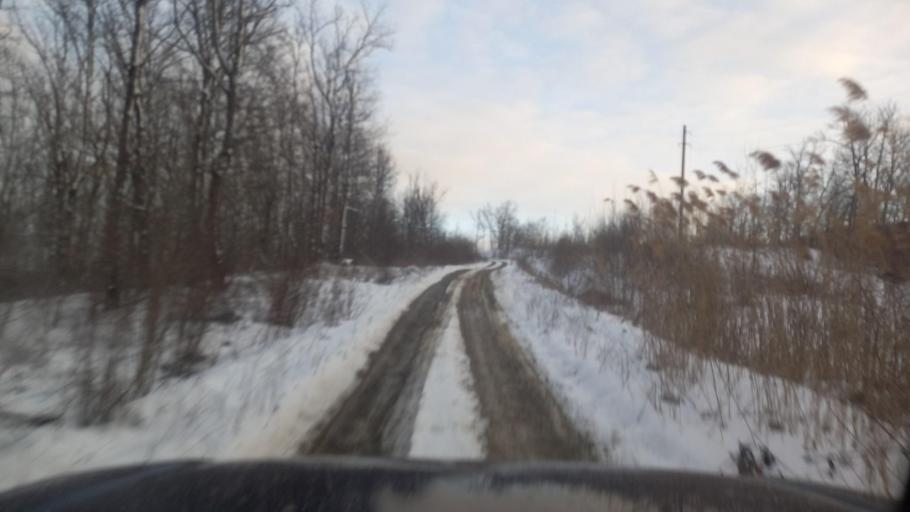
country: RU
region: Krasnodarskiy
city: Smolenskaya
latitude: 44.6766
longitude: 38.7958
